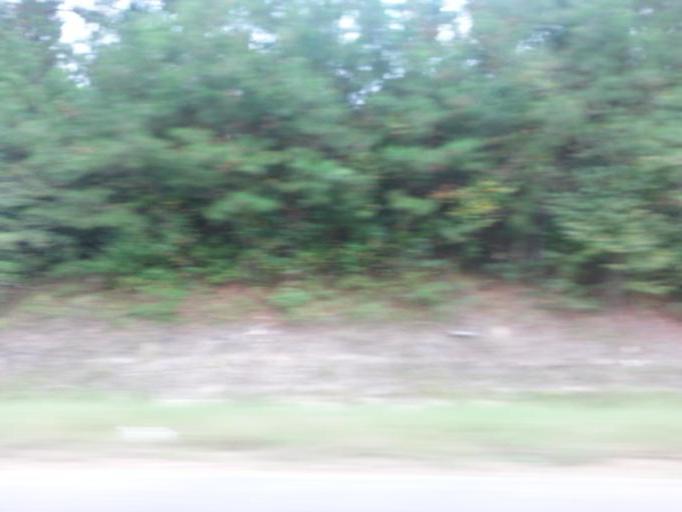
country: US
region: Alabama
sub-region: Butler County
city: Georgiana
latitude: 31.6455
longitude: -86.7804
